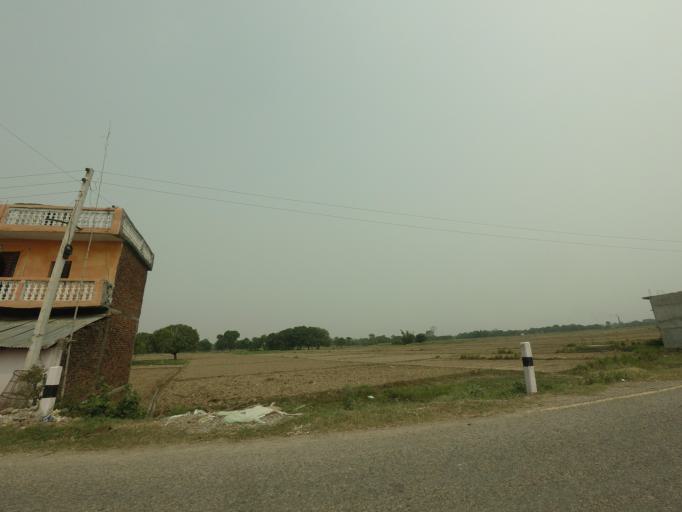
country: IN
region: Uttar Pradesh
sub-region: Maharajganj
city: Nautanwa
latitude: 27.4975
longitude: 83.3290
